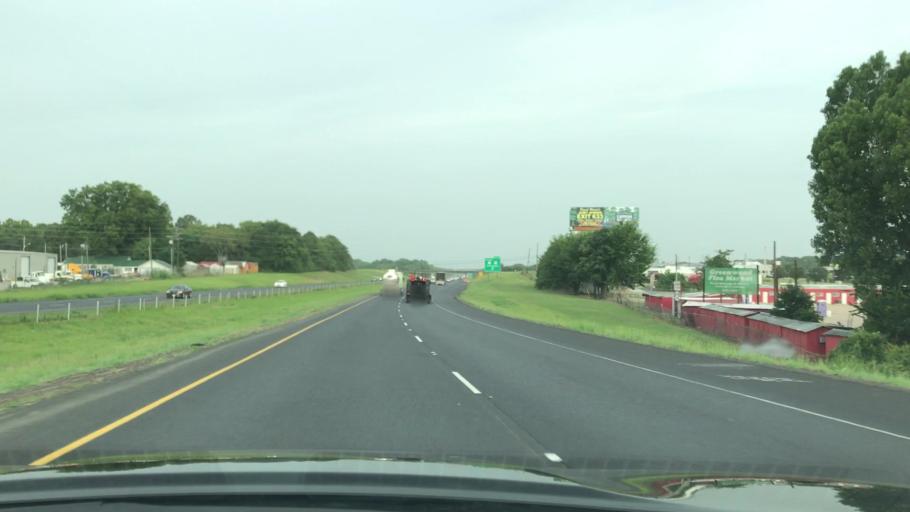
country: US
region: Louisiana
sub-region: Caddo Parish
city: Greenwood
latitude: 32.4437
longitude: -93.9419
